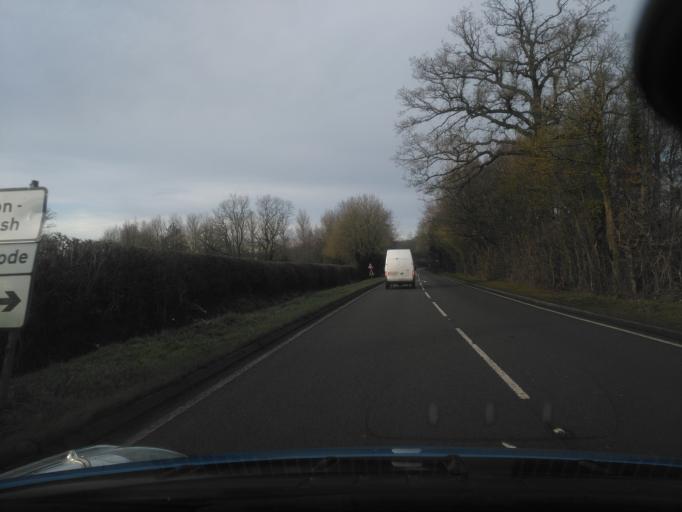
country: GB
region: England
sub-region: Gloucestershire
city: Moreton in Marsh
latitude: 51.9863
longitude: -1.6635
